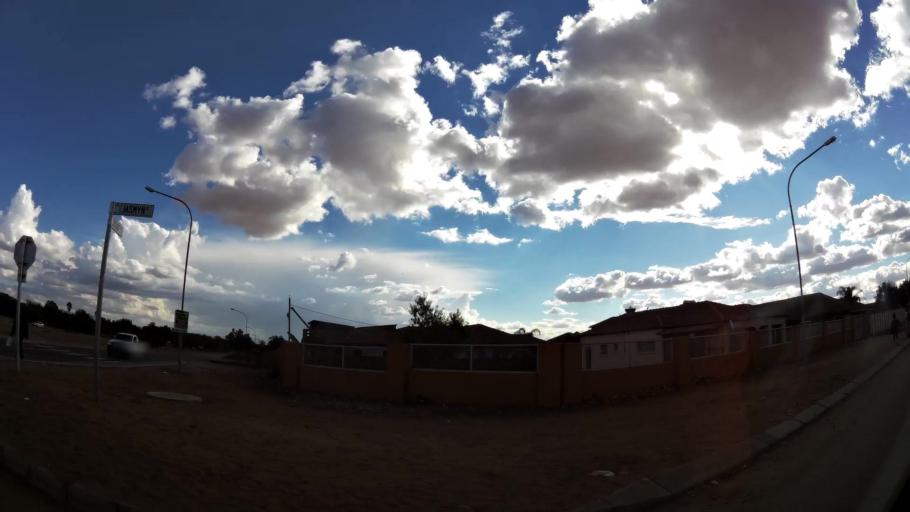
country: ZA
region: Limpopo
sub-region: Capricorn District Municipality
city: Polokwane
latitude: -23.9125
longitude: 29.4962
